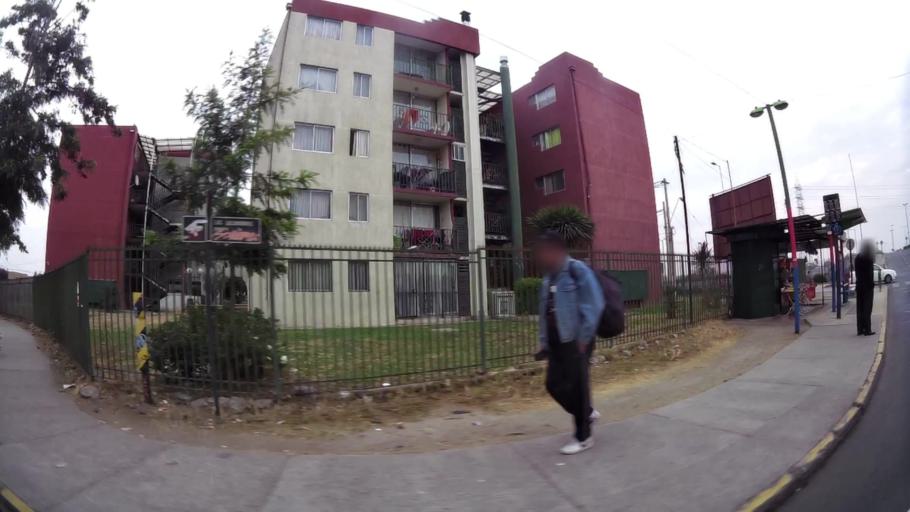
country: CL
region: Santiago Metropolitan
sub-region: Provincia de Santiago
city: Lo Prado
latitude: -33.4855
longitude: -70.7379
